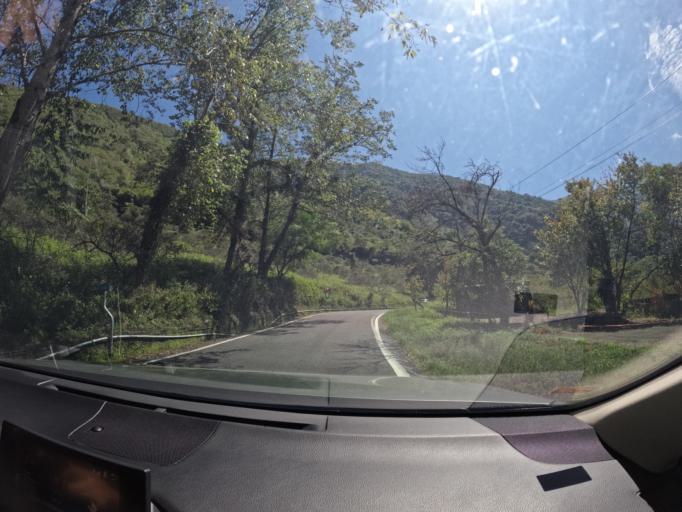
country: TW
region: Taiwan
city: Yujing
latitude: 23.2641
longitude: 120.8490
